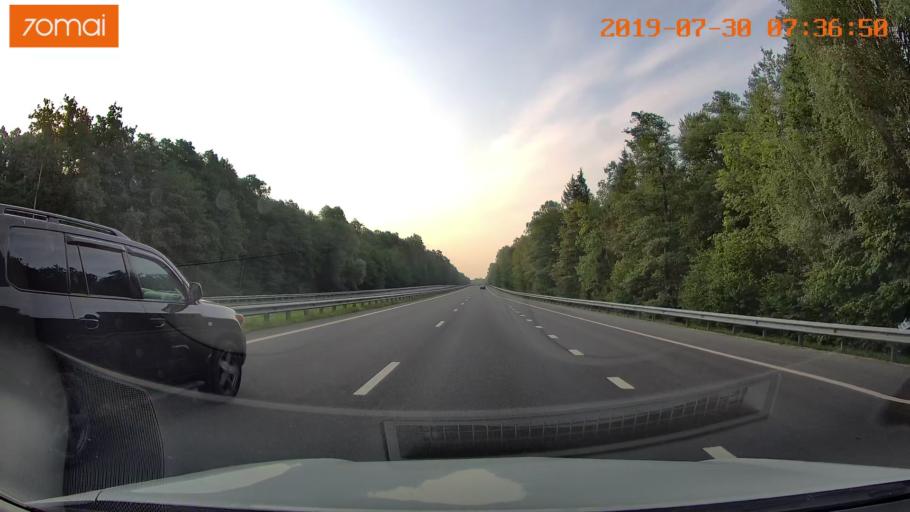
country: RU
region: Kaliningrad
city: Gvardeysk
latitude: 54.6610
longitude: 21.1331
